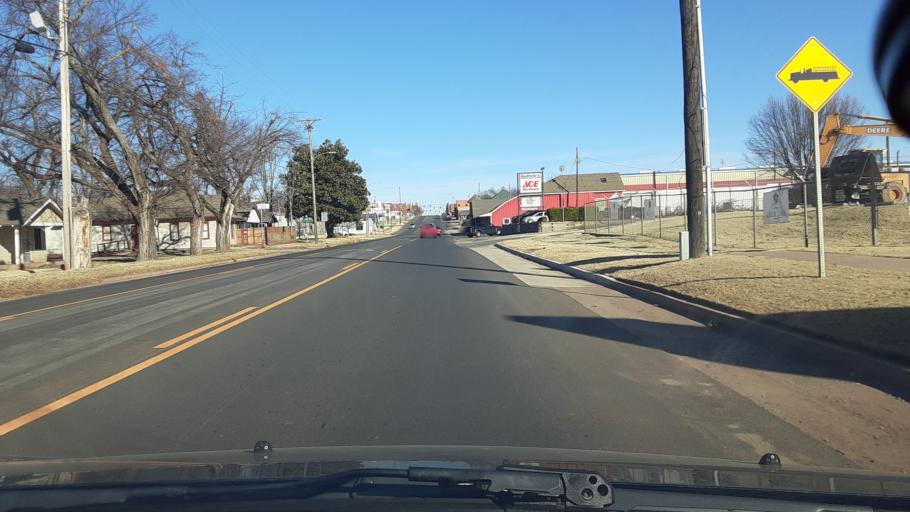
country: US
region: Oklahoma
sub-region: Logan County
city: Guthrie
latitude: 35.8723
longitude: -97.4253
